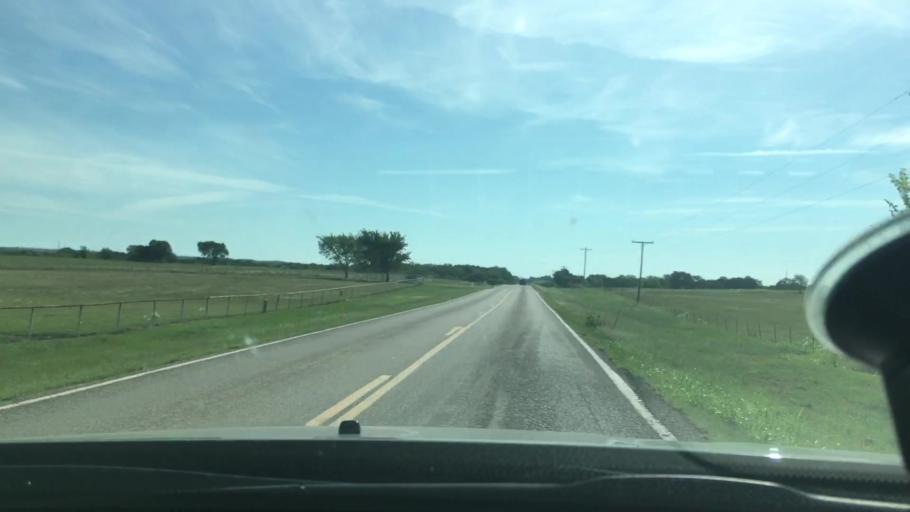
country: US
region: Oklahoma
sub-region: Carter County
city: Ardmore
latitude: 34.3327
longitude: -97.1696
